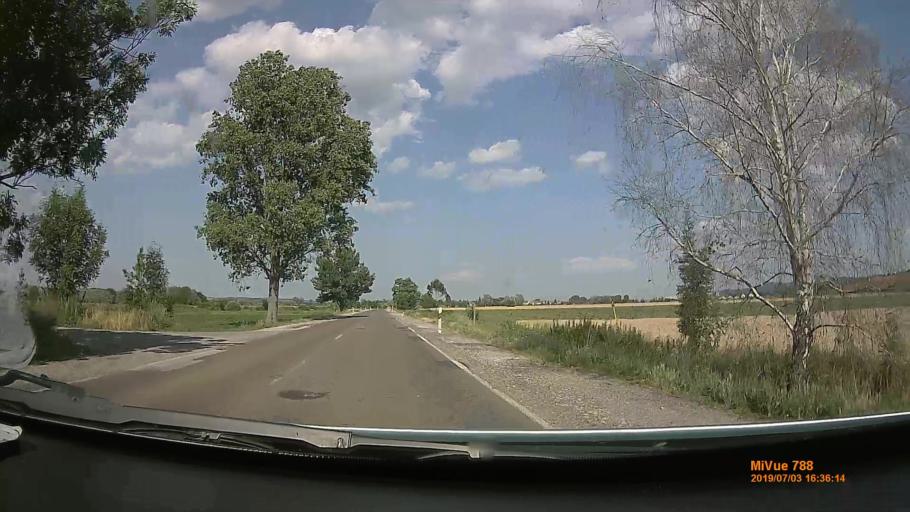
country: HU
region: Borsod-Abauj-Zemplen
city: Sajokaza
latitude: 48.2742
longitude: 20.5649
